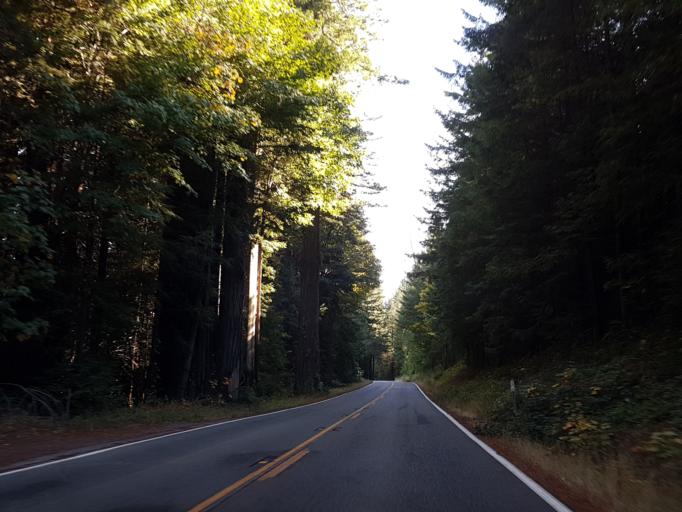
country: US
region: California
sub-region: Humboldt County
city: Rio Dell
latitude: 40.4304
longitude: -123.9843
